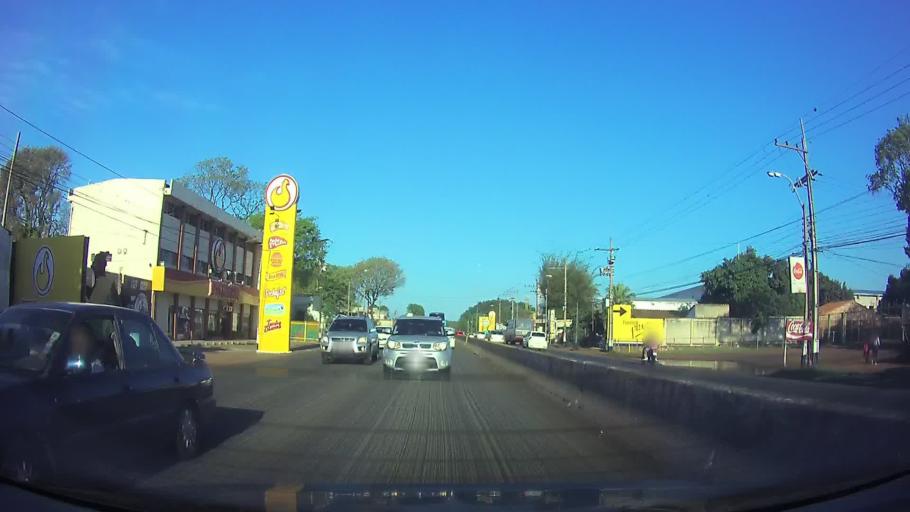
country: PY
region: Central
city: Capiata
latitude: -25.3473
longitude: -57.4701
